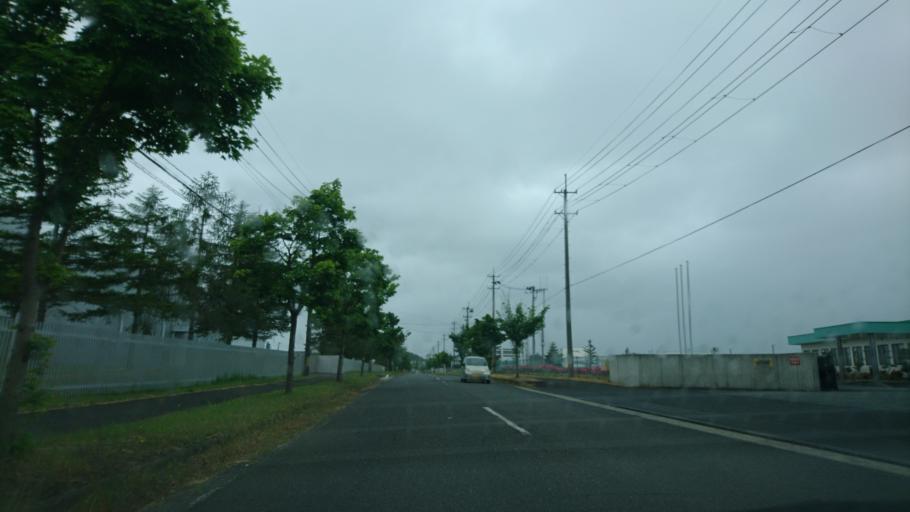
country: JP
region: Iwate
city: Ichinoseki
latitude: 38.9189
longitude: 141.1645
